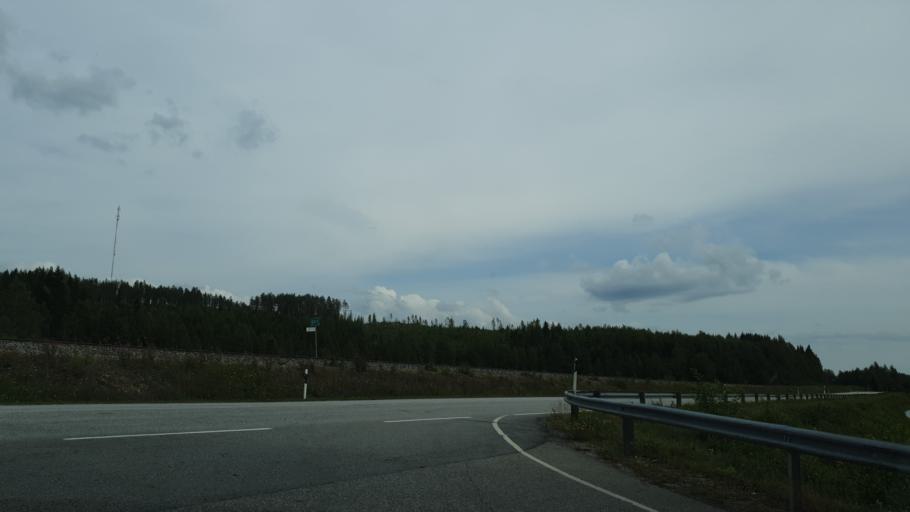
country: FI
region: North Karelia
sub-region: Pielisen Karjala
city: Valtimo
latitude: 63.7022
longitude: 28.7684
